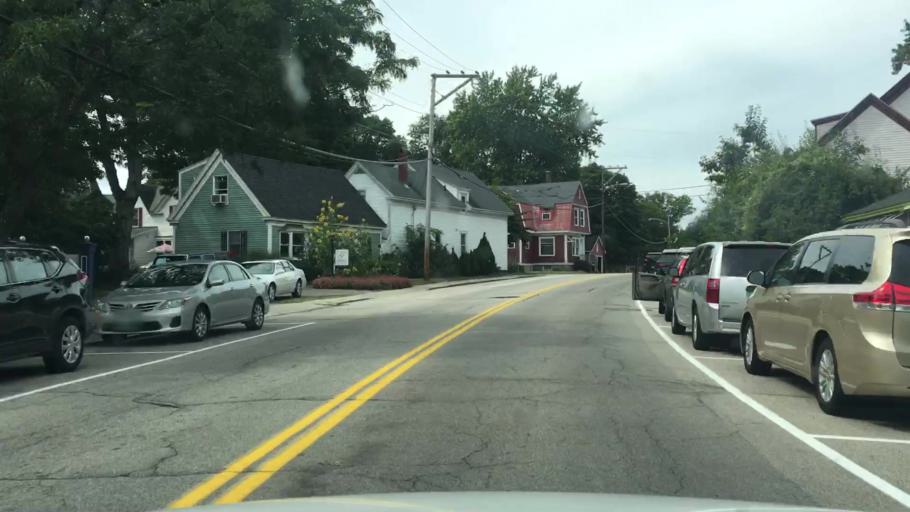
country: US
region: Maine
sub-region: York County
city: Kittery
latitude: 43.0863
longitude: -70.7449
